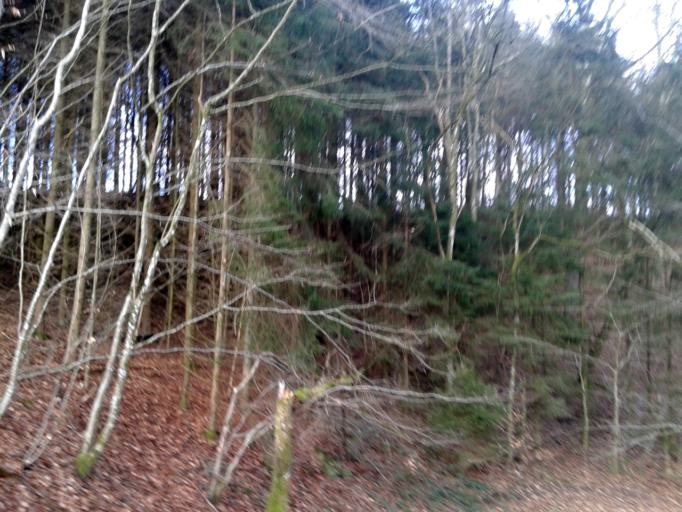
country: LU
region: Luxembourg
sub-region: Canton de Mersch
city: Tuntange
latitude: 49.7036
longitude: 6.0164
